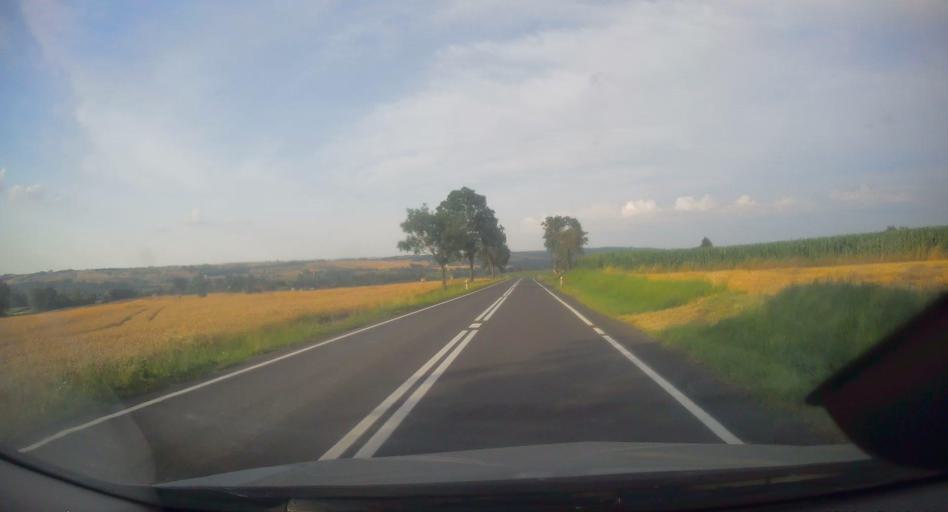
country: PL
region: Swietokrzyskie
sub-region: Powiat kazimierski
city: Bejsce
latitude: 50.1544
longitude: 20.5310
